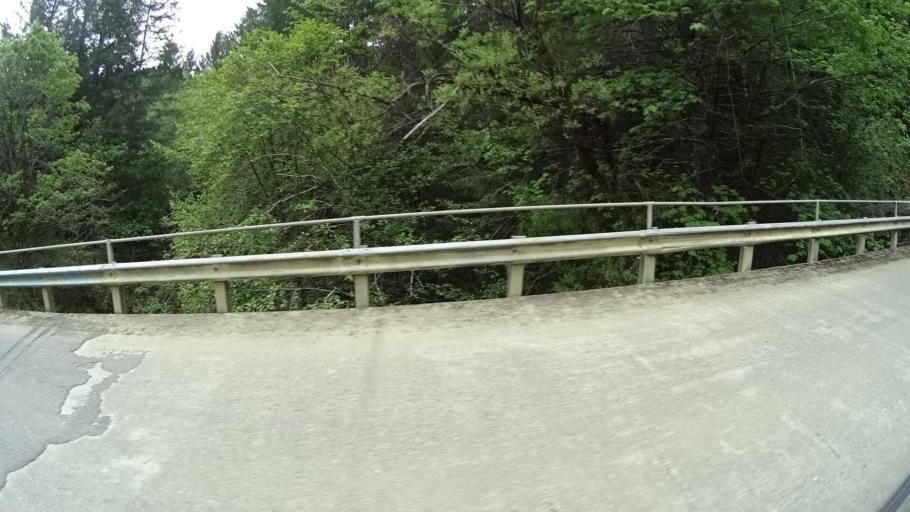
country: US
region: California
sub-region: Humboldt County
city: Redway
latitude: 40.1013
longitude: -123.9169
